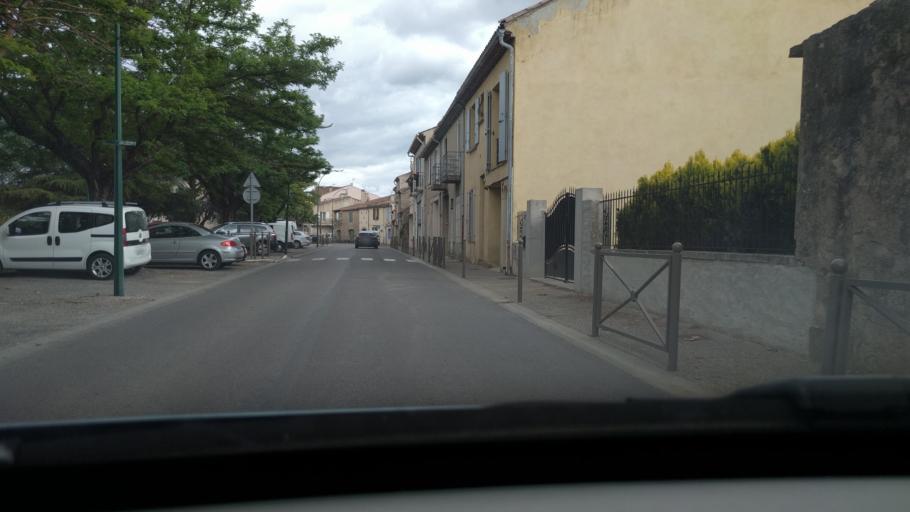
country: FR
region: Provence-Alpes-Cote d'Azur
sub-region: Departement du Vaucluse
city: Grambois
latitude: 43.7269
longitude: 5.5454
